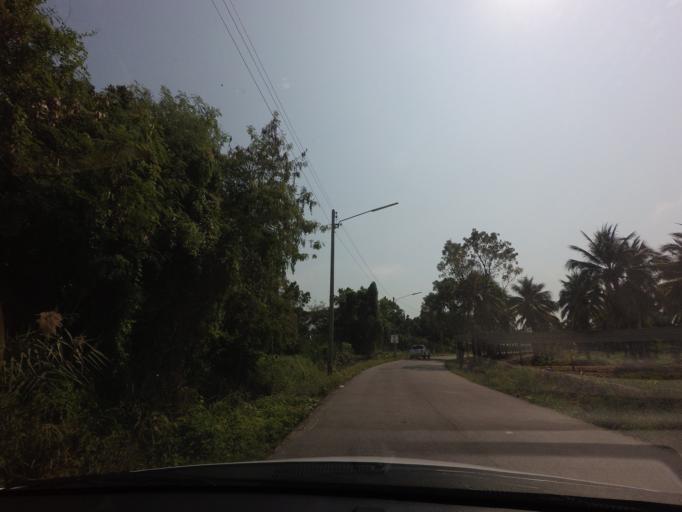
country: TH
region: Nakhon Pathom
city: Sam Phran
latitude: 13.7351
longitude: 100.2646
